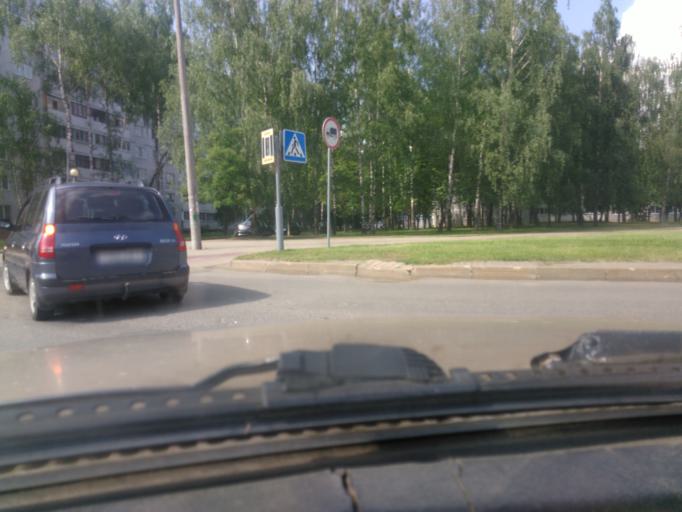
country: BY
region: Mogilev
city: Mahilyow
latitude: 53.9319
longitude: 30.3641
